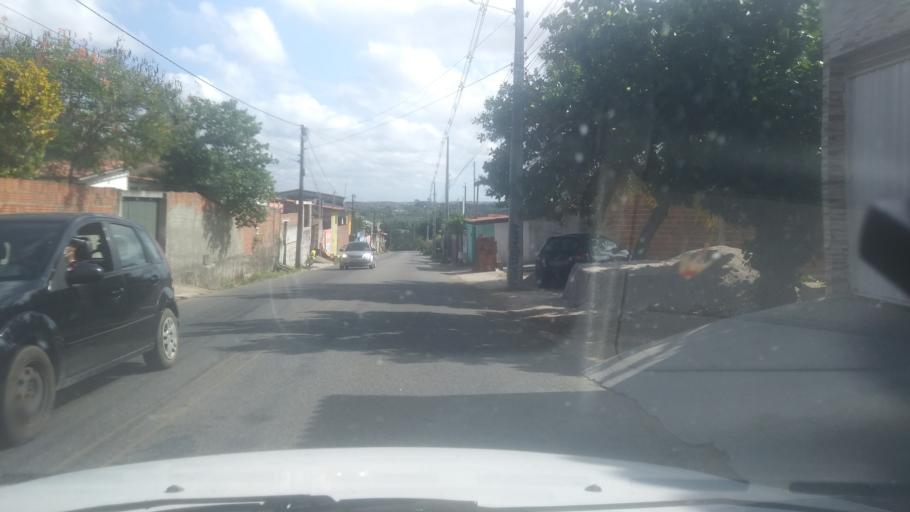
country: BR
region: Rio Grande do Norte
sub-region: Extremoz
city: Extremoz
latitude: -5.7125
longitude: -35.2776
